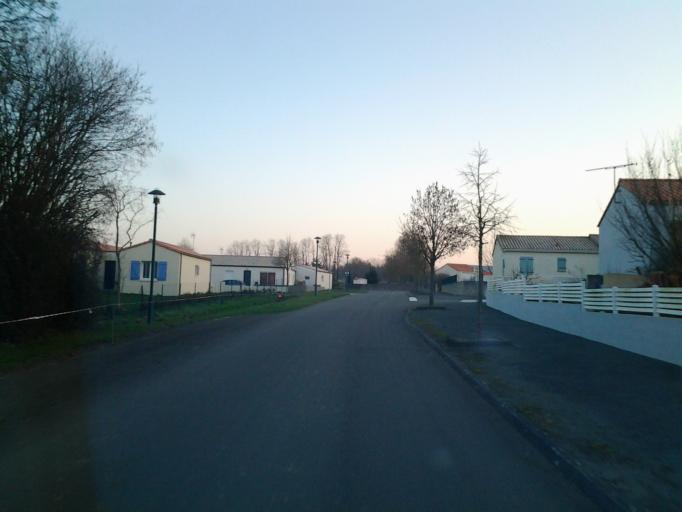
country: FR
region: Pays de la Loire
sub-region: Departement de la Vendee
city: La Chaize-le-Vicomte
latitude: 46.6586
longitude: -1.2357
